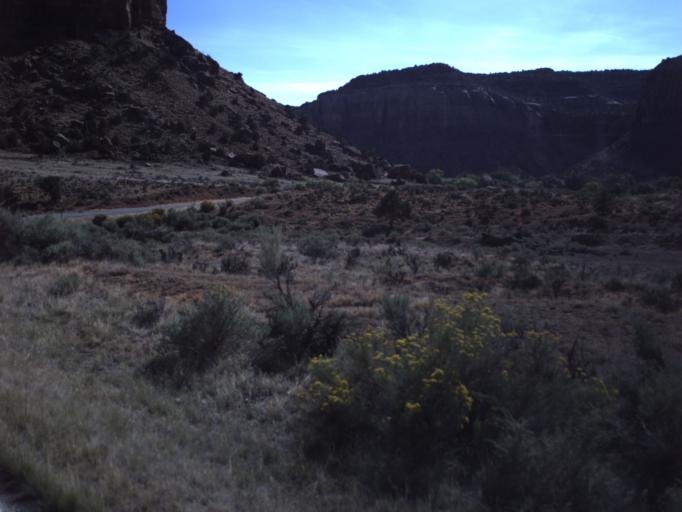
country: US
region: Utah
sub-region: San Juan County
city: Monticello
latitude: 38.0587
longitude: -109.5505
